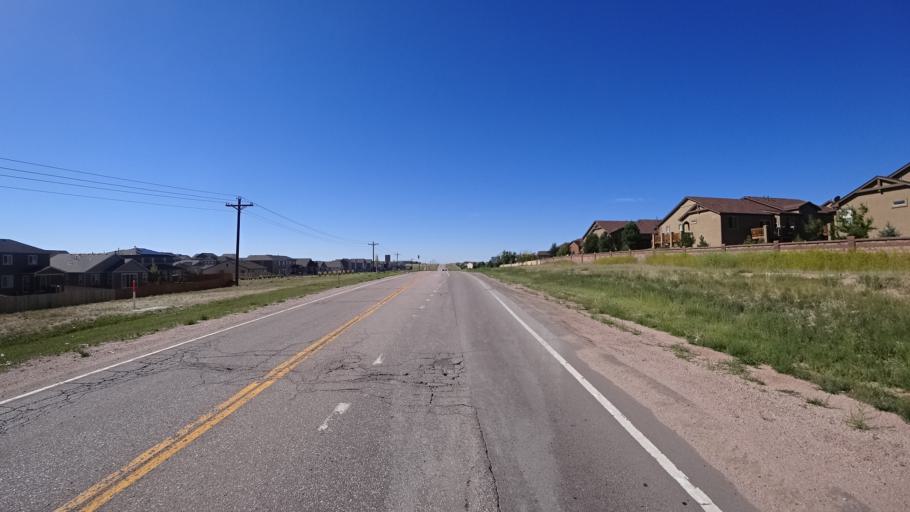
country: US
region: Colorado
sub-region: El Paso County
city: Cimarron Hills
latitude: 38.9226
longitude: -104.6829
